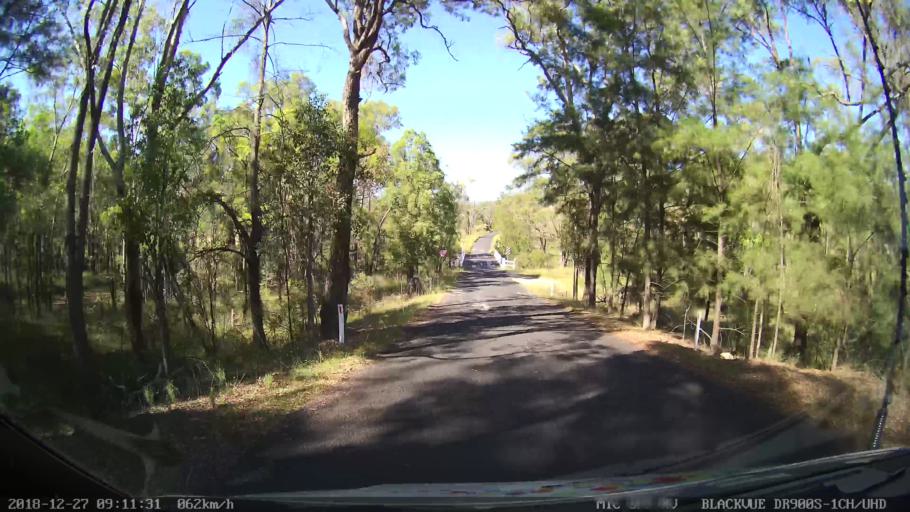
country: AU
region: New South Wales
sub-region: Lithgow
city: Portland
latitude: -33.1362
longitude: 150.1134
